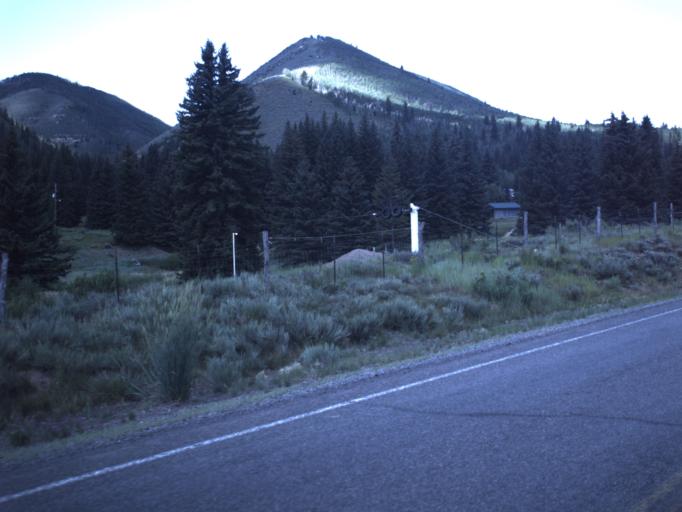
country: US
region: Utah
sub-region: Sanpete County
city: Fairview
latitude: 39.6939
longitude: -111.1562
